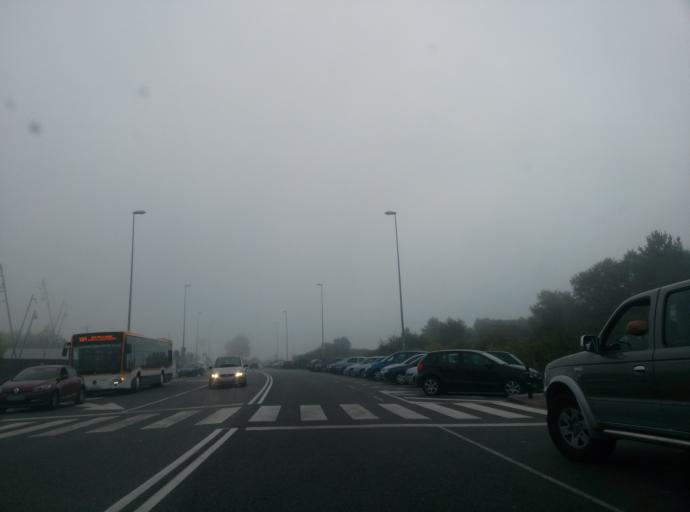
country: ES
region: Galicia
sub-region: Provincia de Lugo
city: Lugo
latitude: 43.0192
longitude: -7.5336
